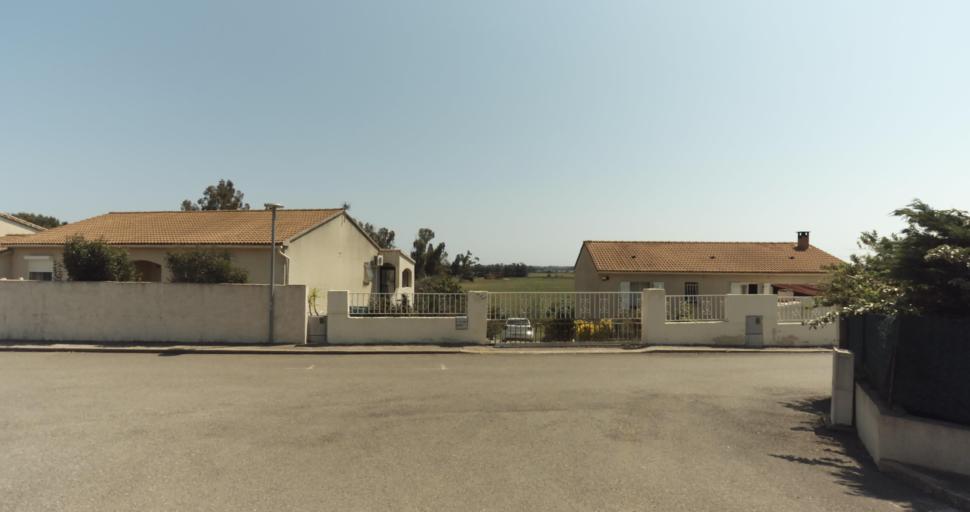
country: FR
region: Corsica
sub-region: Departement de la Haute-Corse
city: Biguglia
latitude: 42.6069
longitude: 9.4333
